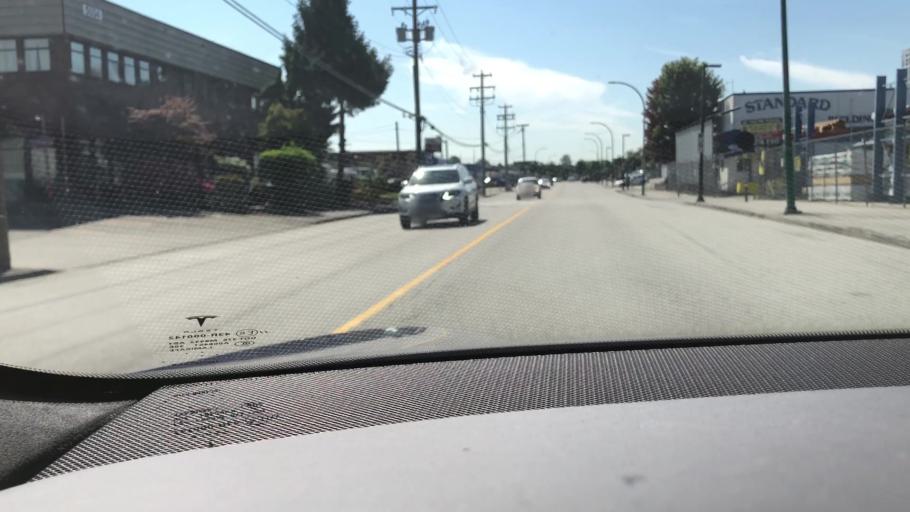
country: CA
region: British Columbia
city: Burnaby
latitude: 49.2608
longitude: -122.9911
